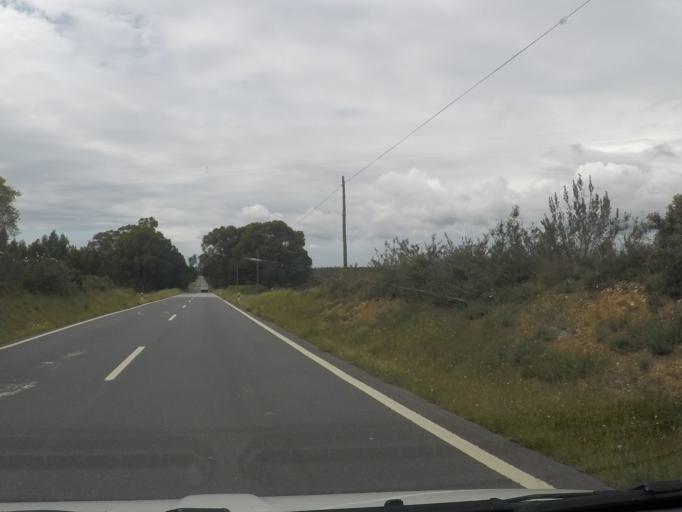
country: PT
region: Setubal
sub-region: Sines
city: Porto Covo
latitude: 37.8815
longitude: -8.7474
